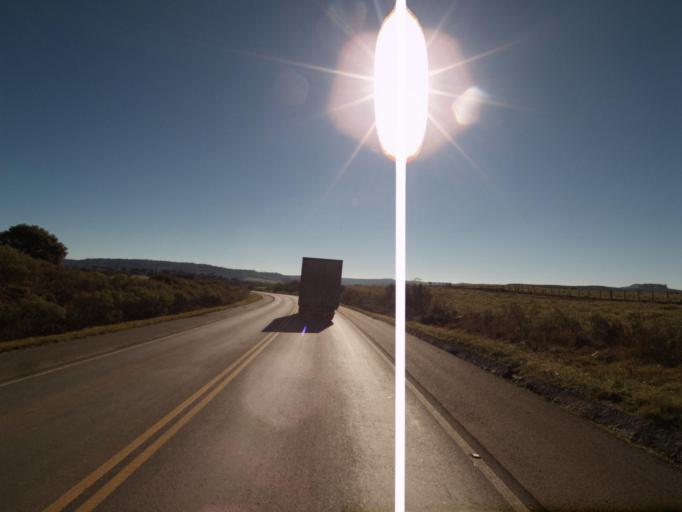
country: BR
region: Santa Catarina
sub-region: Concordia
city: Concordia
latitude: -26.9471
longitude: -51.8249
